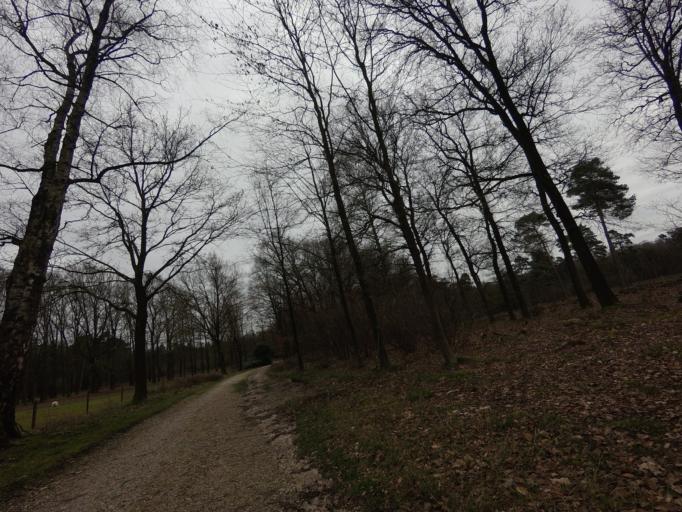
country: NL
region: Utrecht
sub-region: Gemeente Utrechtse Heuvelrug
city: Maarn
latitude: 52.0506
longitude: 5.3659
